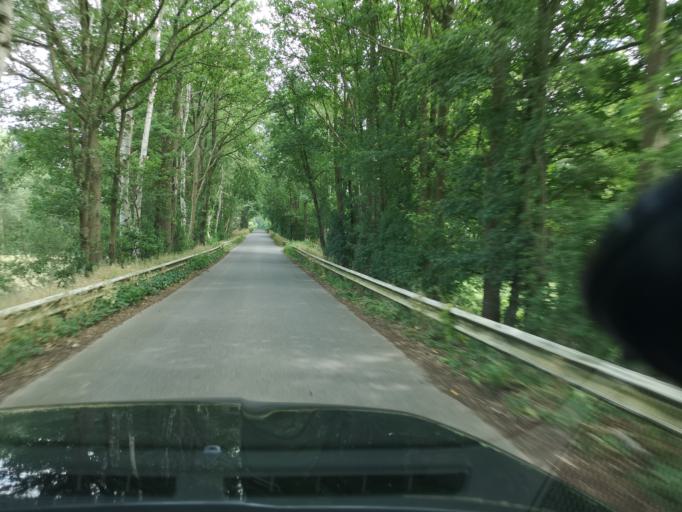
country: DE
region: North Rhine-Westphalia
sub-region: Regierungsbezirk Dusseldorf
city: Wesel
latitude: 51.7050
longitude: 6.6302
